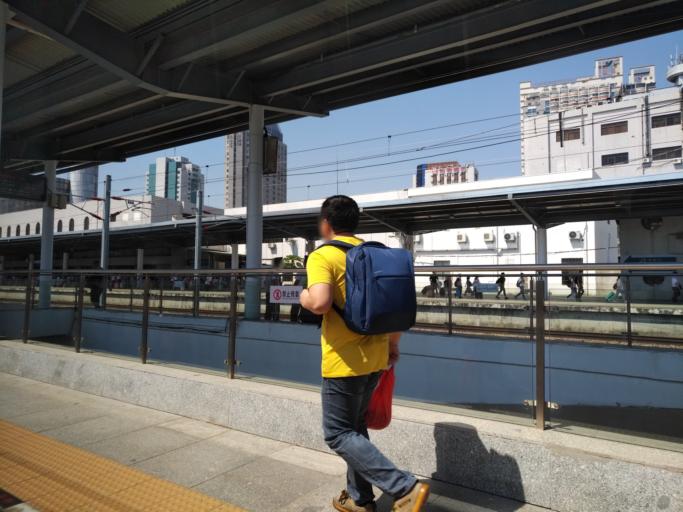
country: CN
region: Guangdong
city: Mazhang
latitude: 21.2457
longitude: 110.2843
